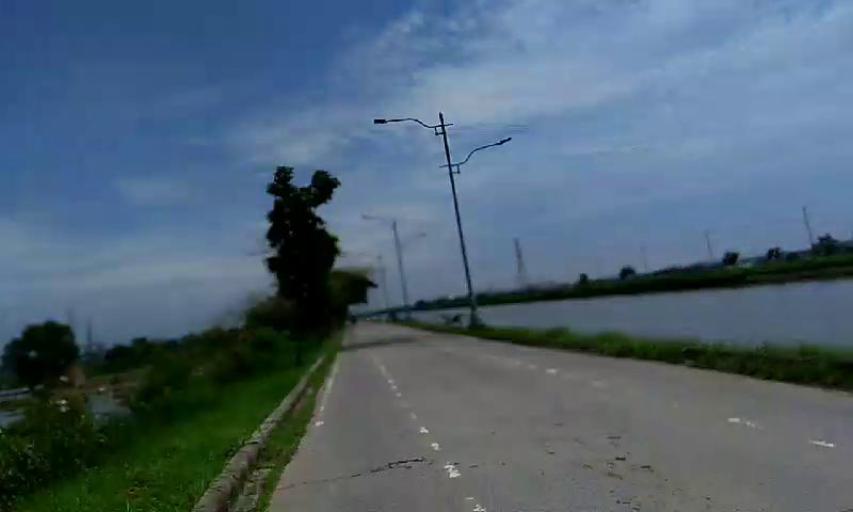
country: ID
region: West Java
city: Bekasi
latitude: -6.1227
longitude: 106.9692
